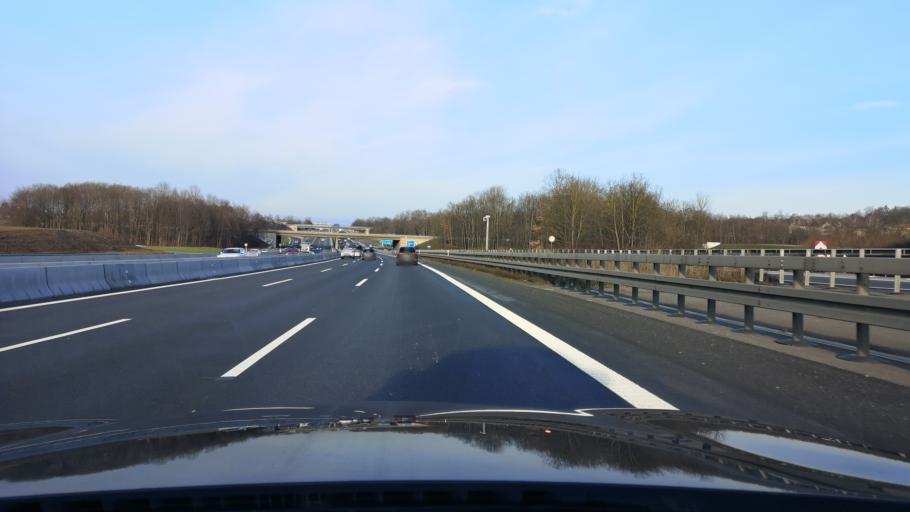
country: DE
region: Baden-Wuerttemberg
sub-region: Regierungsbezirk Stuttgart
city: Korntal
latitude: 48.8485
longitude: 9.1192
